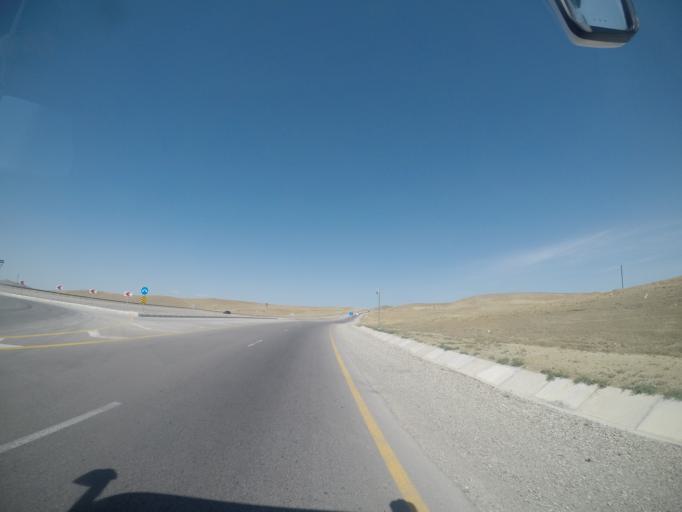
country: AZ
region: Sumqayit
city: Haci Zeynalabdin
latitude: 40.4755
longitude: 49.4551
